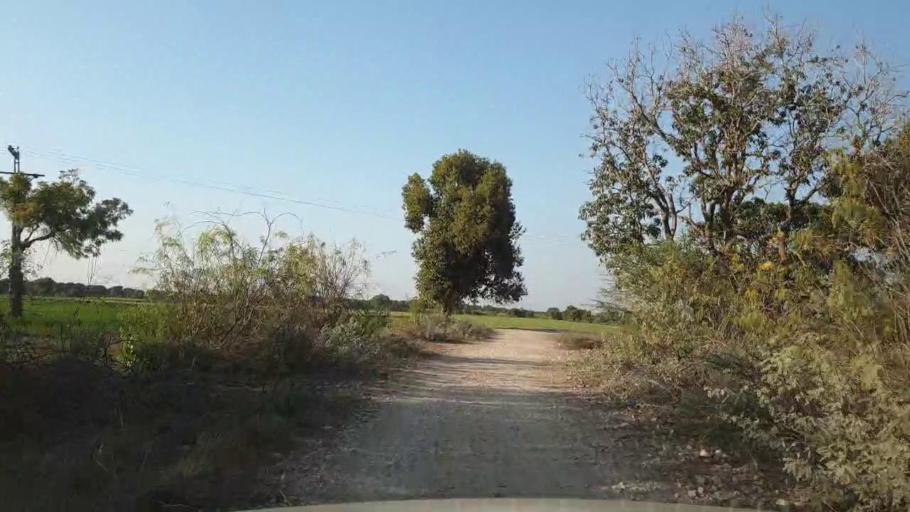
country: PK
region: Sindh
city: Tando Allahyar
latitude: 25.4945
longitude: 68.6419
